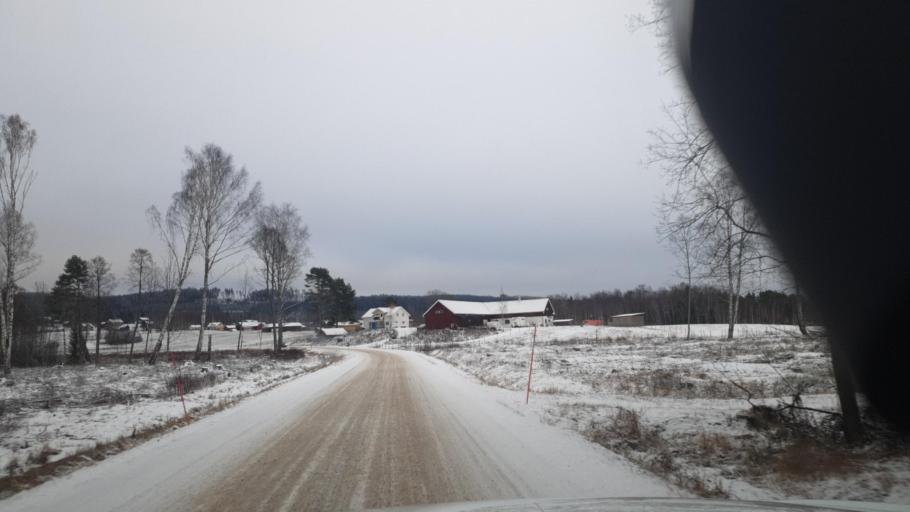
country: SE
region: Vaermland
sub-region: Sunne Kommun
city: Sunne
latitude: 59.7400
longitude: 13.0687
